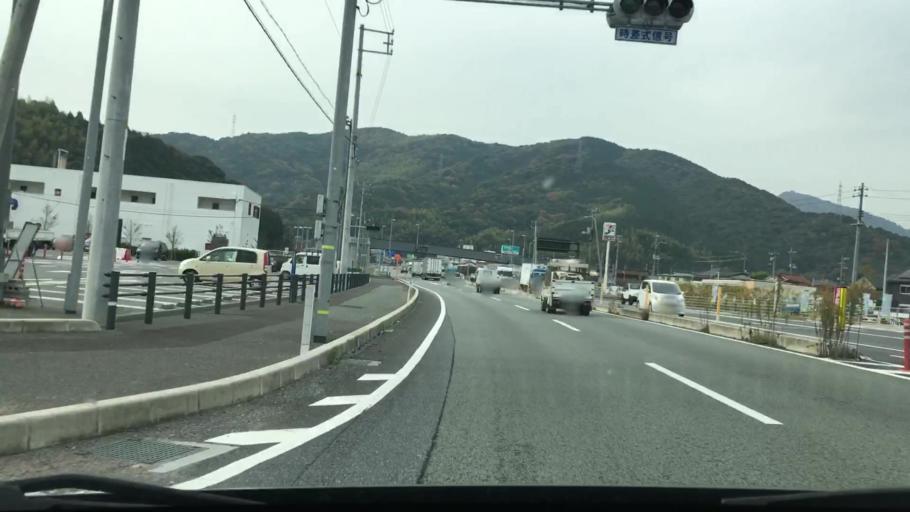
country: JP
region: Yamaguchi
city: Hofu
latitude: 34.0754
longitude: 131.6887
